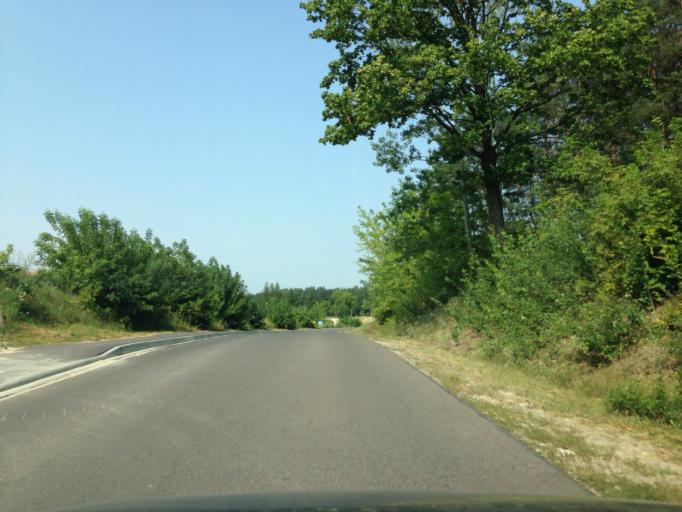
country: PL
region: Kujawsko-Pomorskie
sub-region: Powiat golubsko-dobrzynski
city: Golub-Dobrzyn
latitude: 53.0735
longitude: 19.0316
